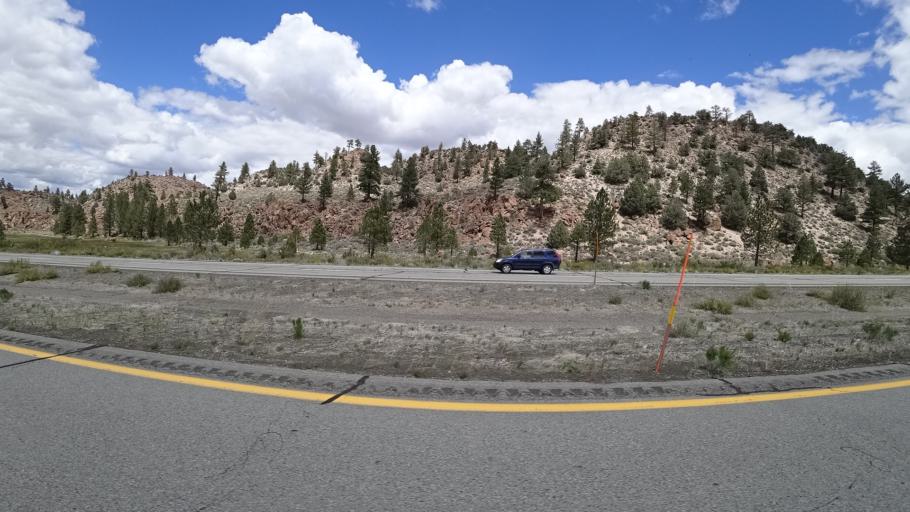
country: US
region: California
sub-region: Mono County
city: Mammoth Lakes
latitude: 37.5659
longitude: -118.6885
